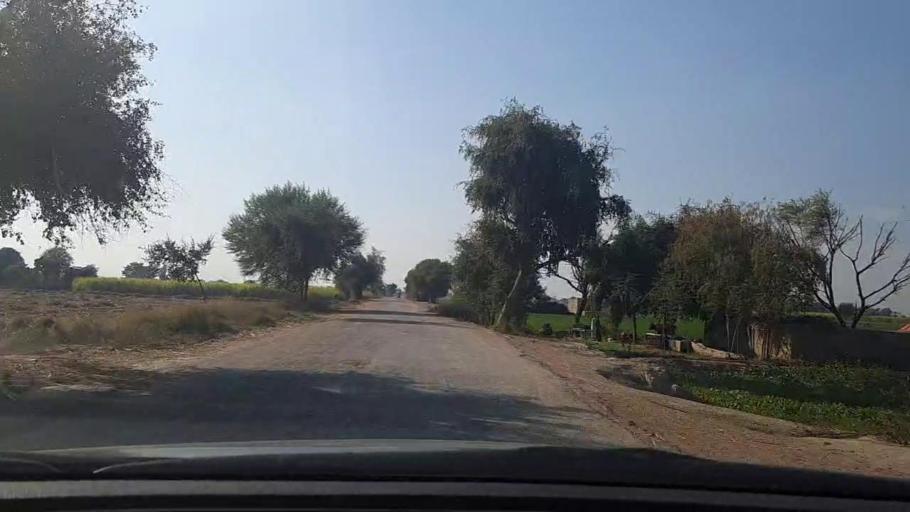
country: PK
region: Sindh
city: Daulatpur
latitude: 26.3207
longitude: 68.0322
